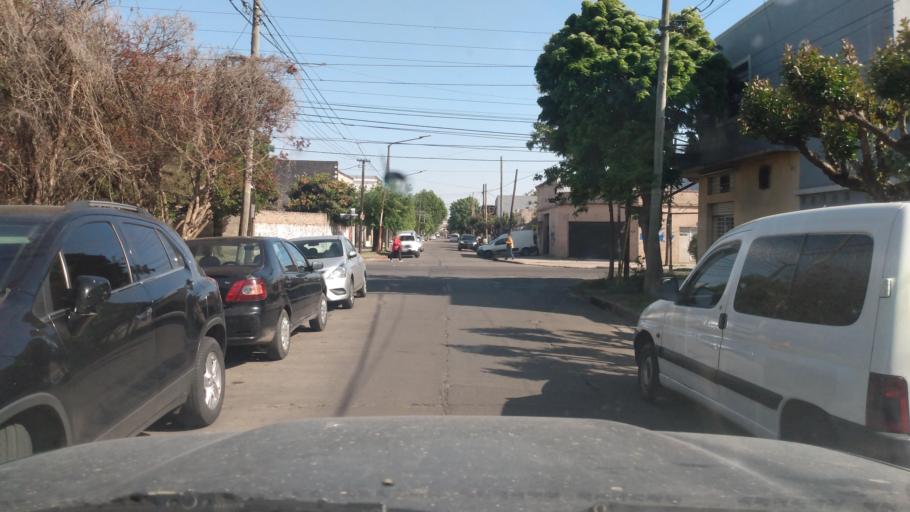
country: AR
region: Buenos Aires
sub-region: Partido de Moron
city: Moron
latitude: -34.6538
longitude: -58.5968
